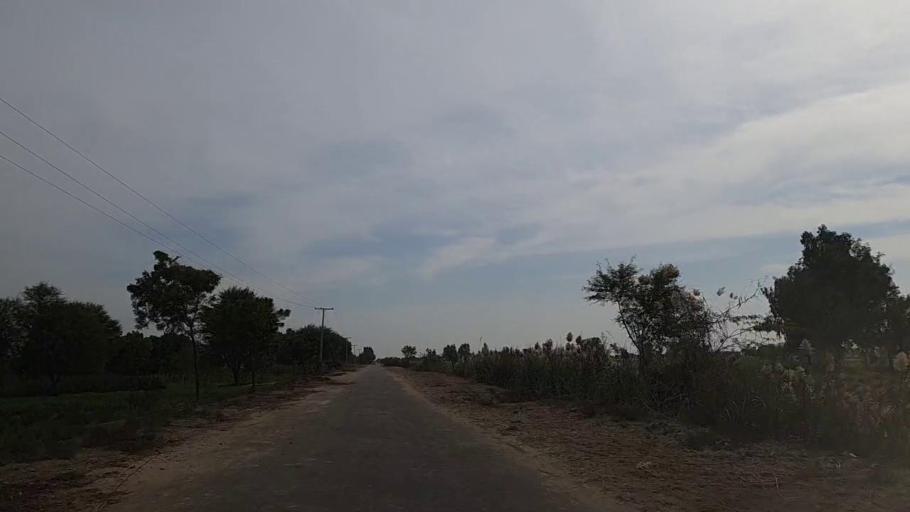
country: PK
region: Sindh
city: Daur
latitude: 26.4275
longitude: 68.4823
